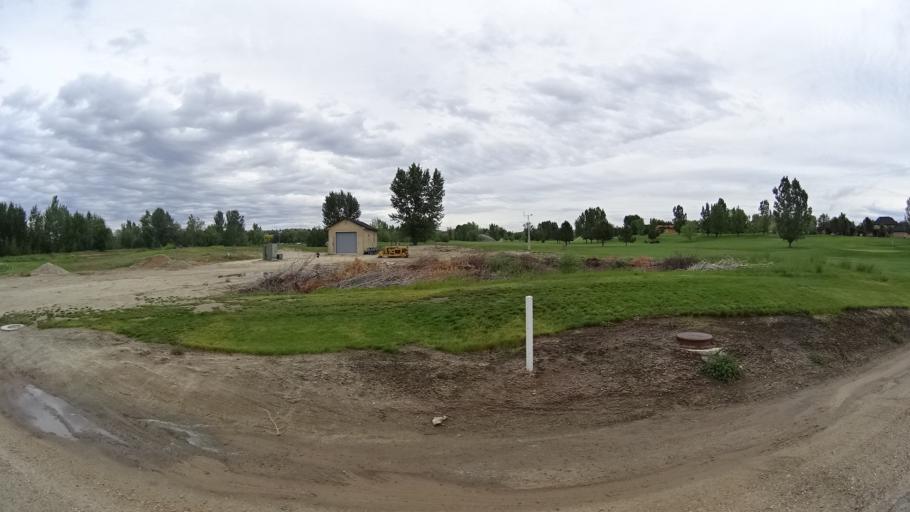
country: US
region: Idaho
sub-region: Ada County
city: Star
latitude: 43.7210
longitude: -116.4664
